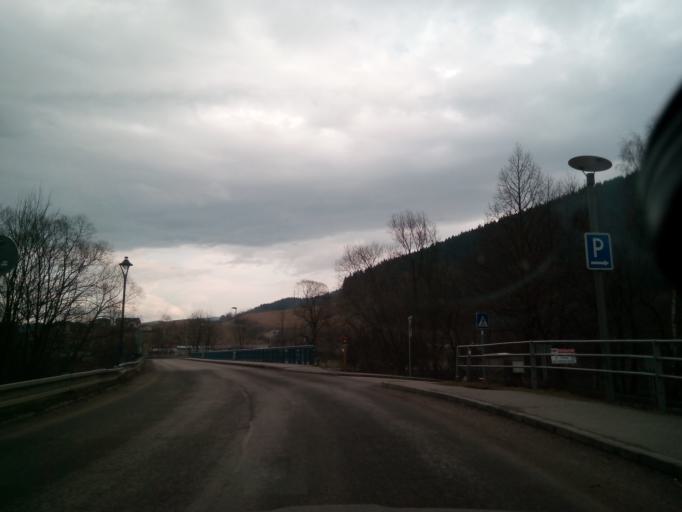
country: SK
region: Zilinsky
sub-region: Okres Dolny Kubin
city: Dolny Kubin
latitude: 49.2607
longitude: 19.3590
